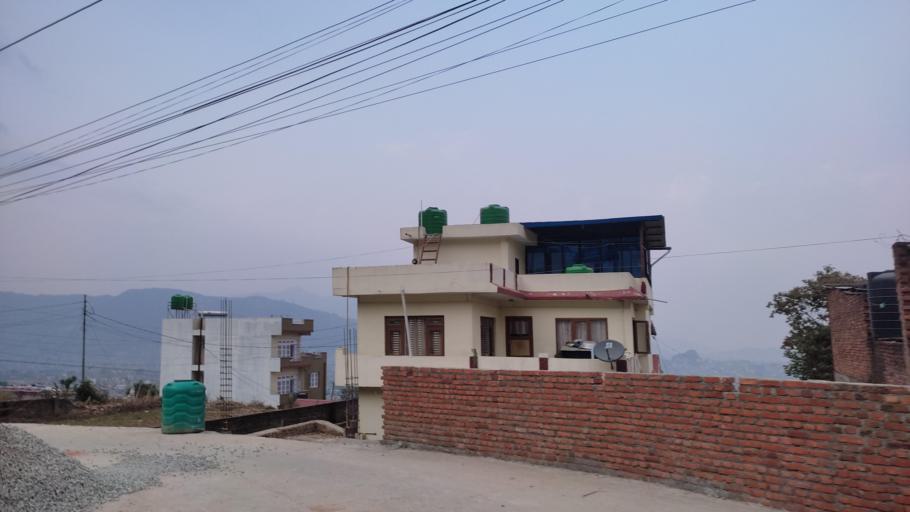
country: NP
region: Central Region
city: Kirtipur
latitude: 27.6705
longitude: 85.2444
